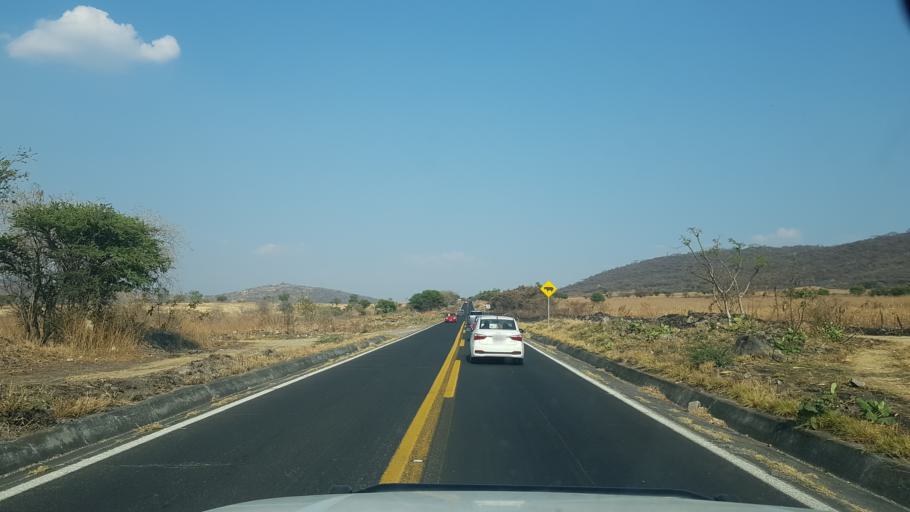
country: MX
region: Puebla
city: Calmeca
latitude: 18.6550
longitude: -98.6610
